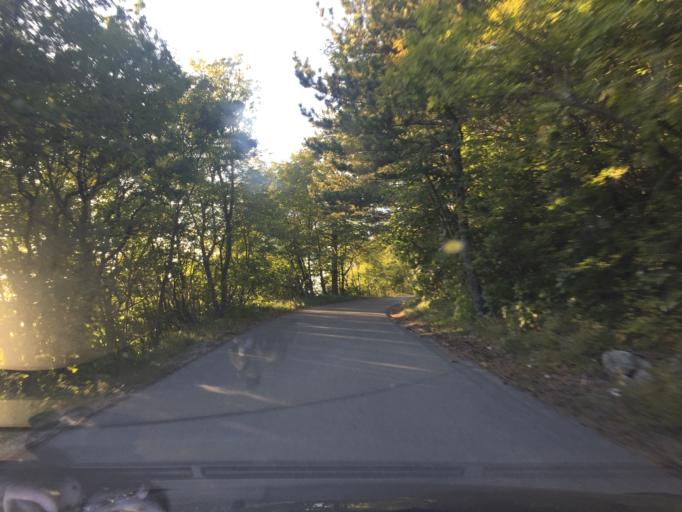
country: SI
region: Vipava
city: Vipava
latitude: 45.7993
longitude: 13.9984
